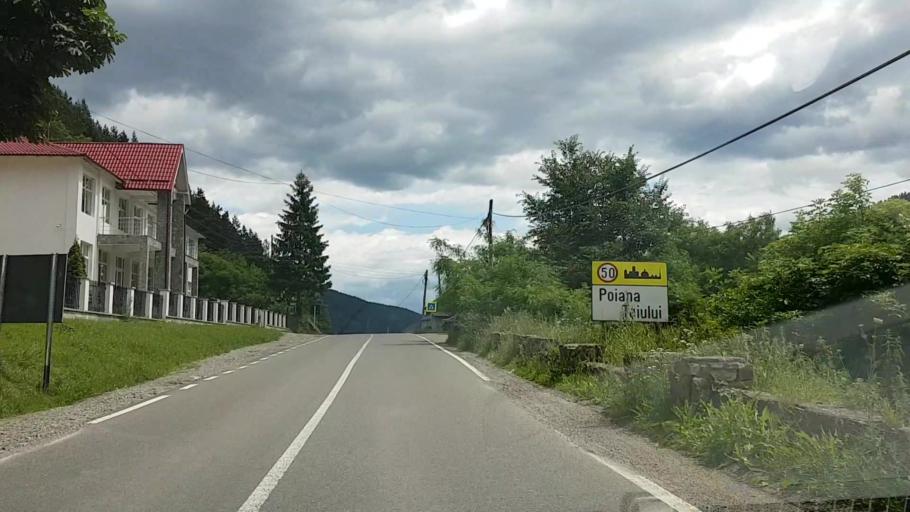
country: RO
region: Neamt
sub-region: Comuna Poiana Teiului
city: Poiana Teiului
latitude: 47.1204
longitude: 25.9119
